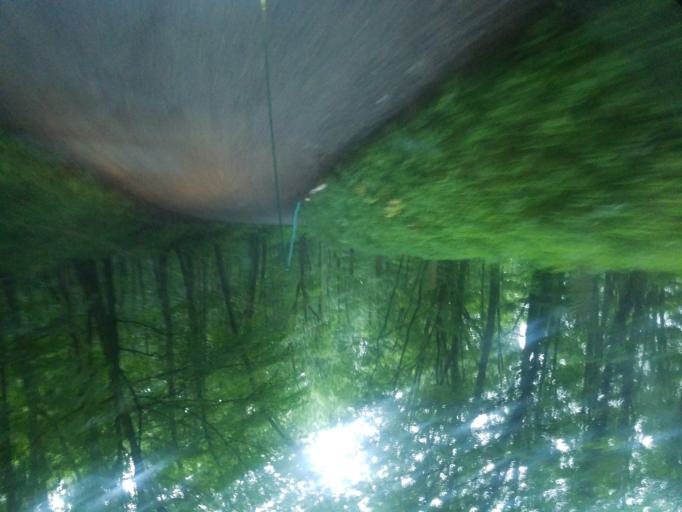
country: US
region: Ohio
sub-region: Columbiana County
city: Salineville
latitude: 40.6183
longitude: -80.8947
